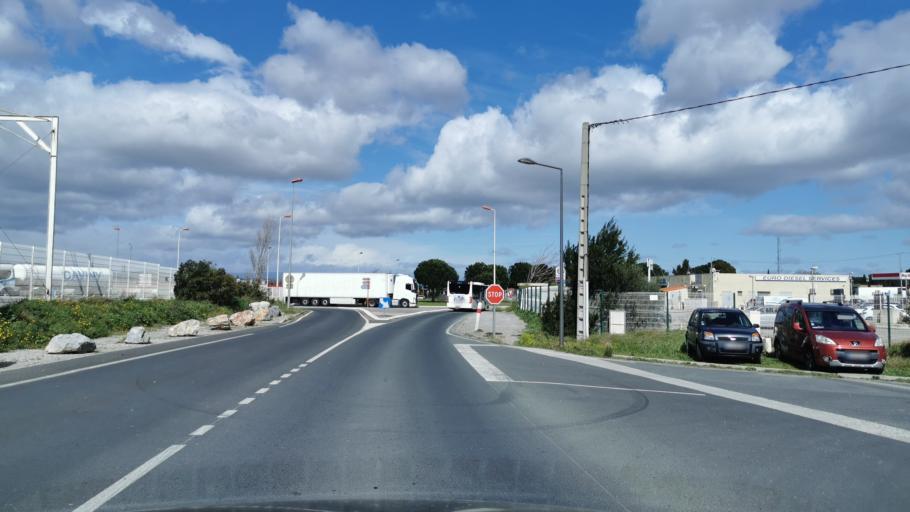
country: FR
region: Languedoc-Roussillon
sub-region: Departement de l'Aude
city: Narbonne
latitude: 43.1615
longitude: 2.9889
